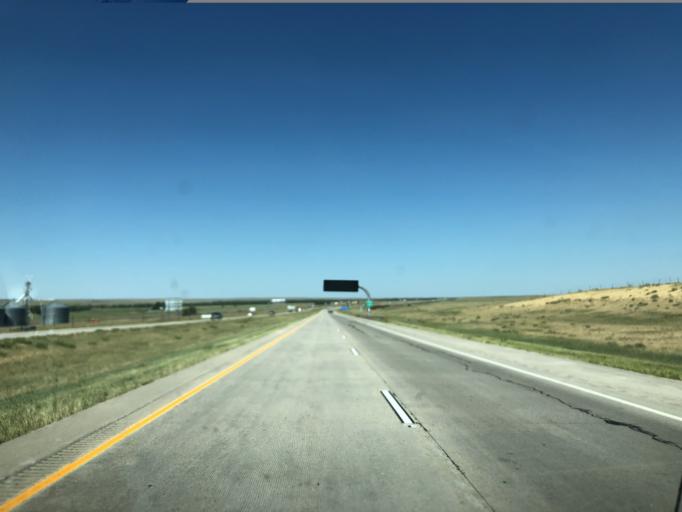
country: US
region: Colorado
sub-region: Lincoln County
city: Limon
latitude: 39.2734
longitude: -103.7220
